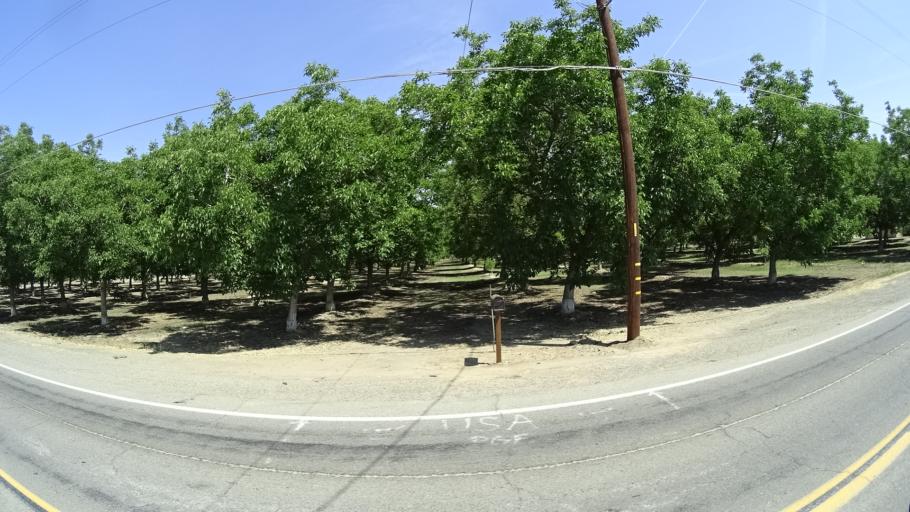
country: US
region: California
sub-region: Fresno County
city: Laton
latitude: 36.4011
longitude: -119.7126
